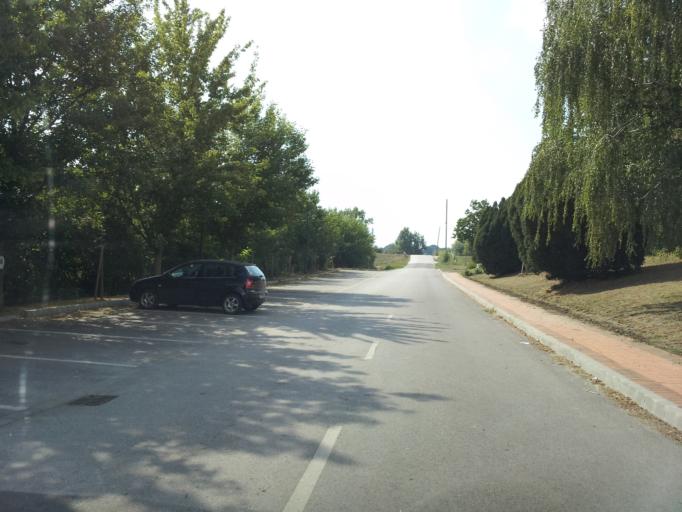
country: HU
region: Pest
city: Toekoel
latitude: 47.3209
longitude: 18.9608
